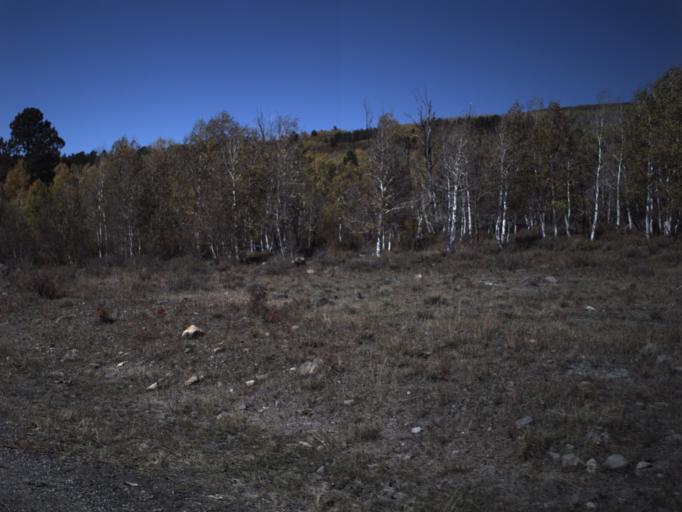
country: US
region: Utah
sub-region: Wayne County
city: Loa
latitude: 38.0088
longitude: -111.4017
